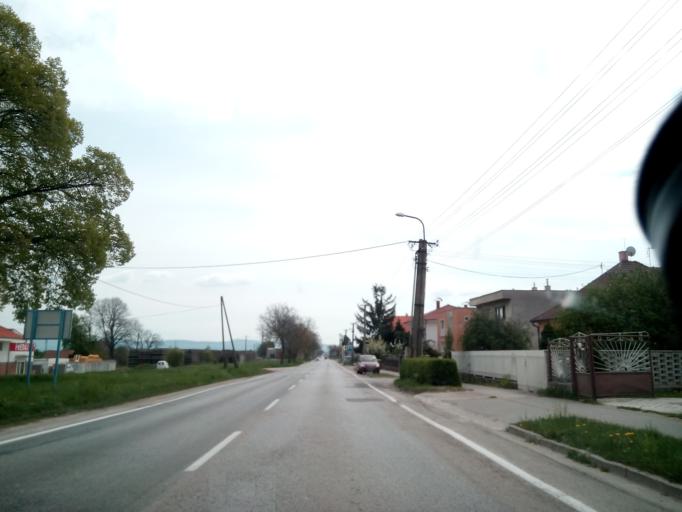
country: SK
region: Trnavsky
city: Vrbove
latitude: 48.6153
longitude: 17.7334
